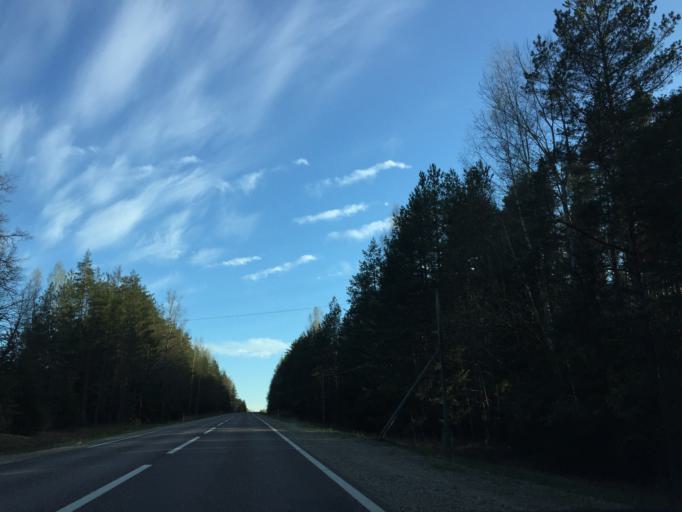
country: LV
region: Valkas Rajons
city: Valka
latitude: 57.7349
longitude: 25.9433
